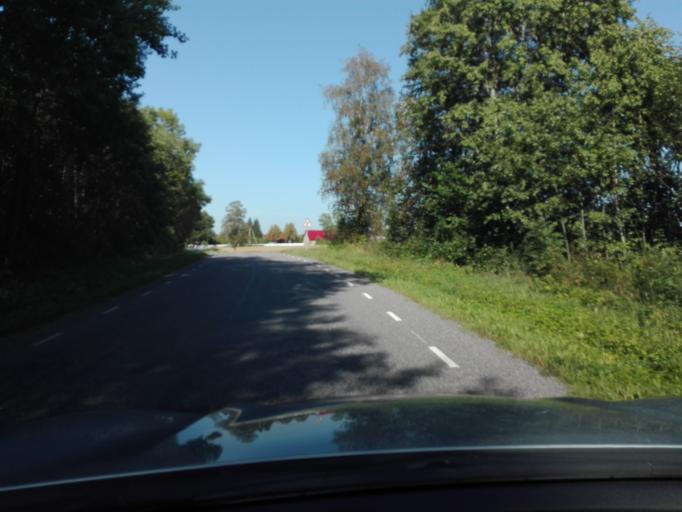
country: EE
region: Raplamaa
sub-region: Rapla vald
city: Rapla
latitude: 59.0229
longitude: 24.7769
